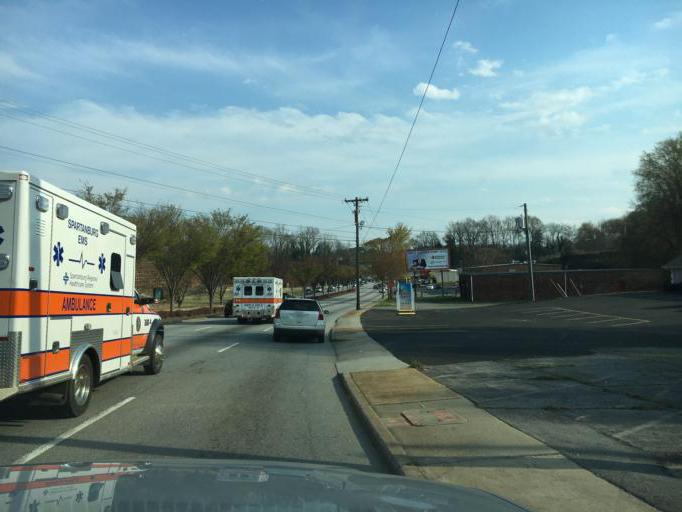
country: US
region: South Carolina
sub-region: Spartanburg County
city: Spartanburg
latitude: 34.9632
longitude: -81.9271
